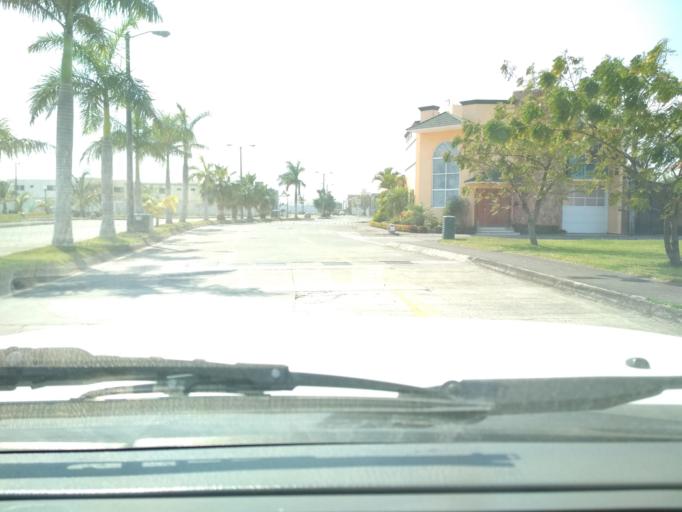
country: MX
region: Veracruz
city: Boca del Rio
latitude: 19.1045
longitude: -96.1229
